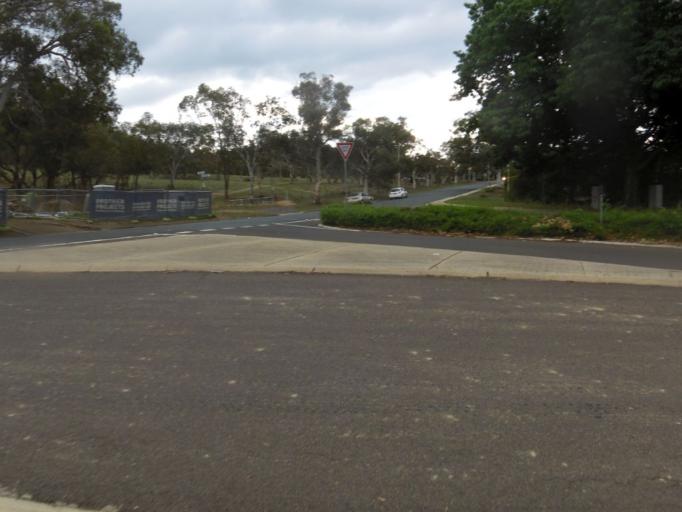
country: AU
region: Australian Capital Territory
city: Forrest
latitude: -35.3374
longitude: 149.1224
